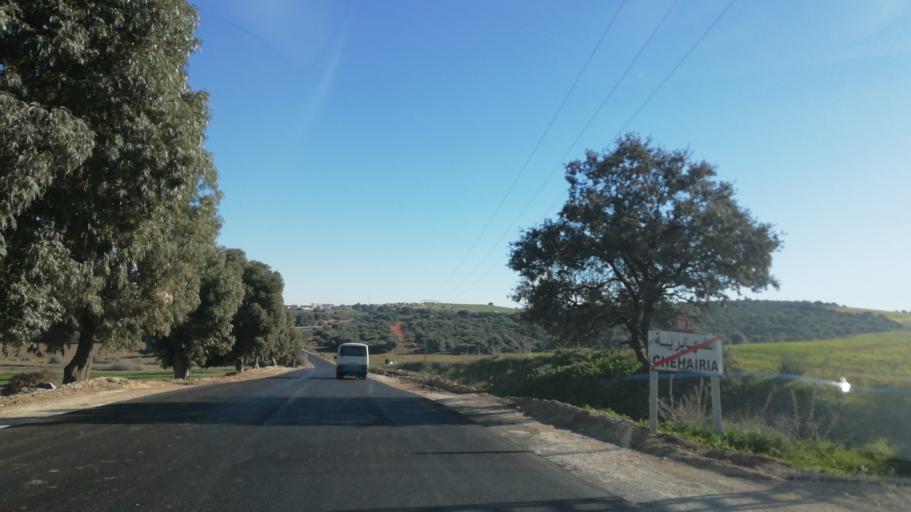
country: DZ
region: Relizane
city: Smala
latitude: 35.6695
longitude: 0.8064
